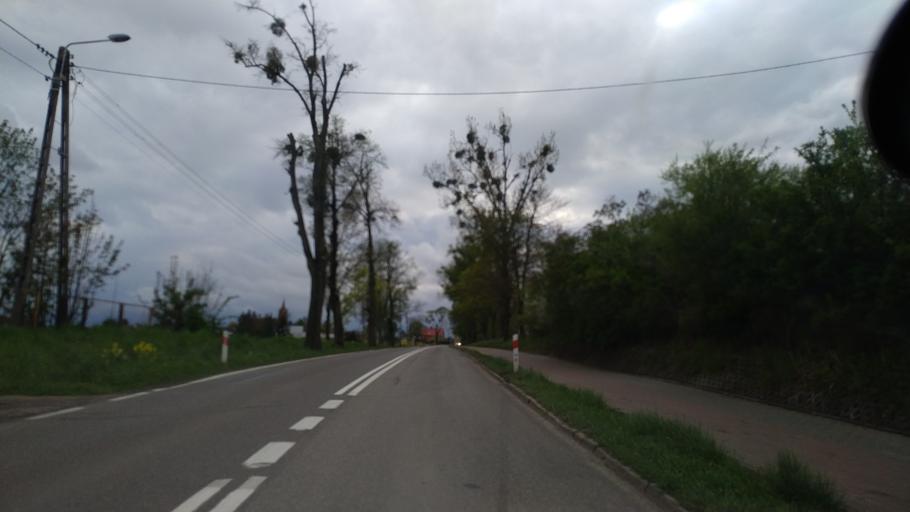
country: PL
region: Pomeranian Voivodeship
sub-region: Powiat kwidzynski
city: Ryjewo
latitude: 53.7837
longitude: 18.9613
